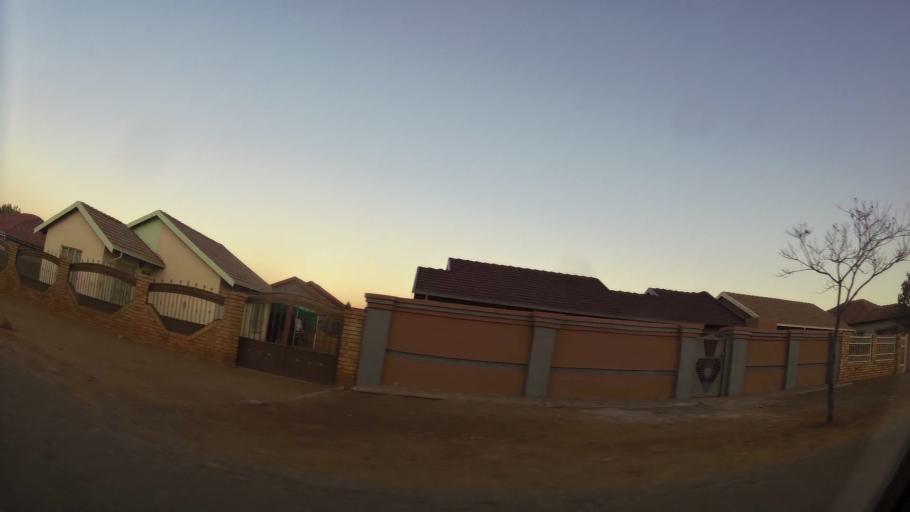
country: ZA
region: North-West
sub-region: Bojanala Platinum District Municipality
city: Rustenburg
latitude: -25.6476
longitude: 27.2078
